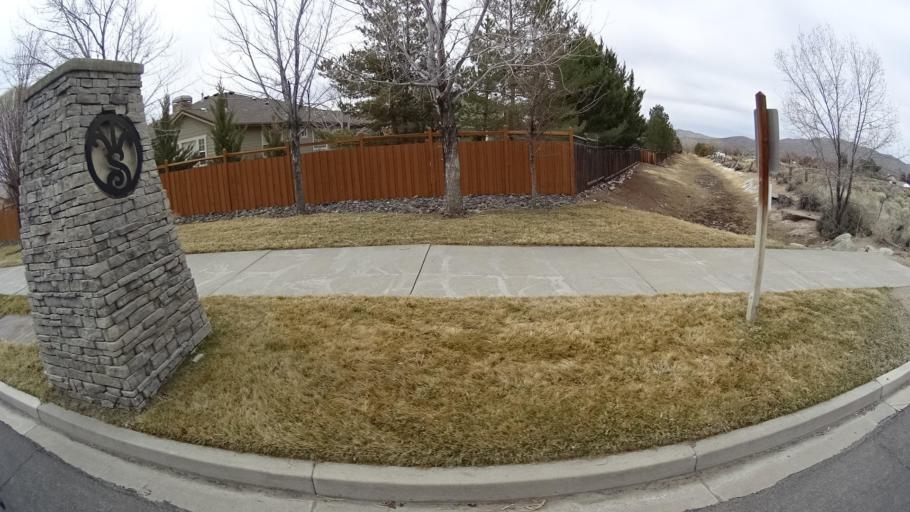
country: US
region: Nevada
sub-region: Washoe County
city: Spanish Springs
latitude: 39.6253
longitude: -119.6865
